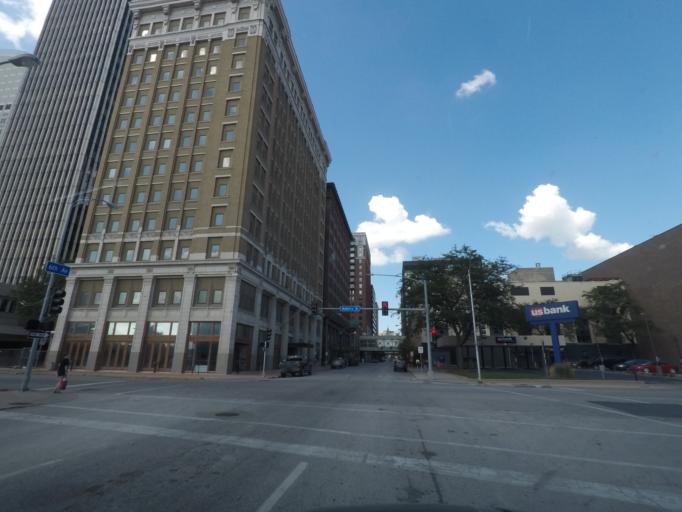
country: US
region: Iowa
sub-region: Polk County
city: Des Moines
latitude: 41.5848
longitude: -93.6242
